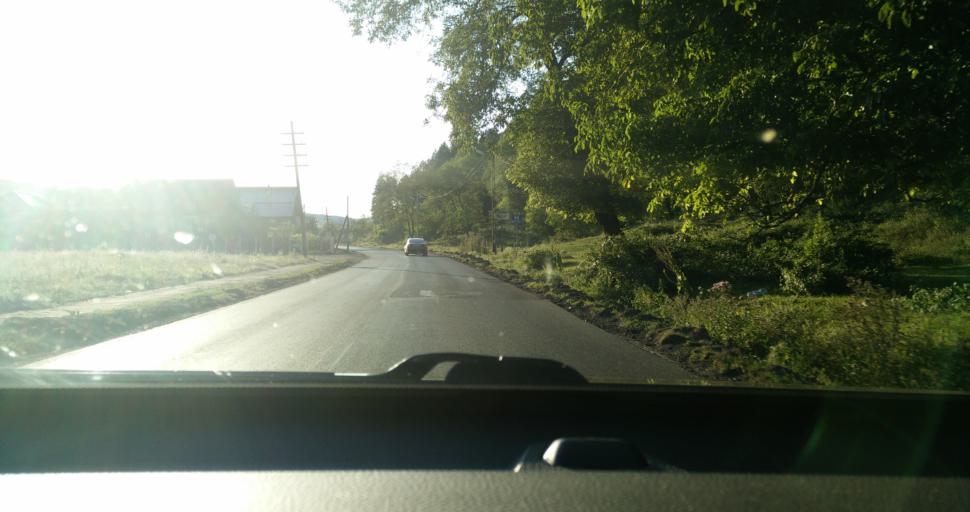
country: RO
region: Bihor
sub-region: Oras Nucet
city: Nucet
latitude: 46.4840
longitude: 22.5694
